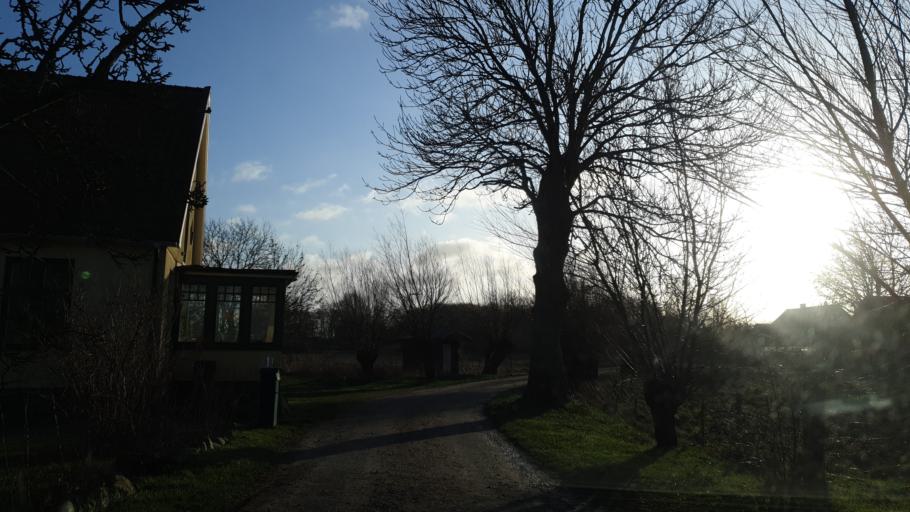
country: SE
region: Skane
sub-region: Malmo
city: Tygelsjo
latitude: 55.5030
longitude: 13.0281
